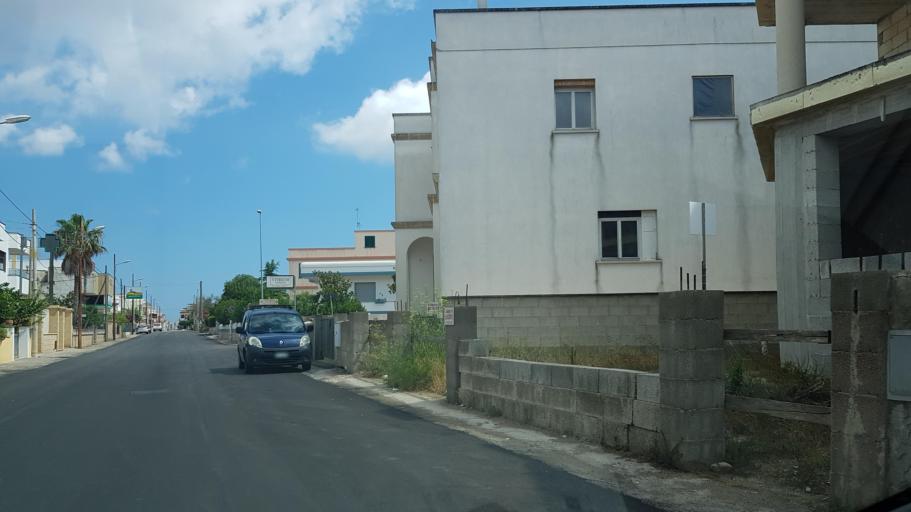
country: IT
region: Apulia
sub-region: Provincia di Lecce
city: Patu
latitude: 39.8398
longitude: 18.3427
